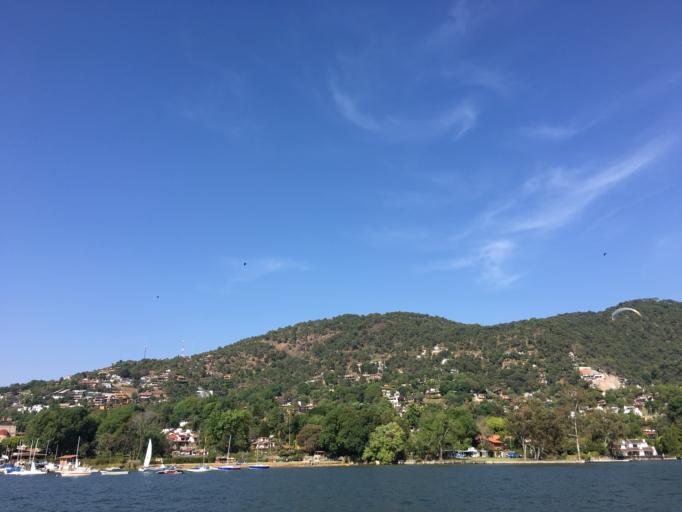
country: MX
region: Mexico
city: Valle de Bravo
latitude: 19.1815
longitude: -100.1290
